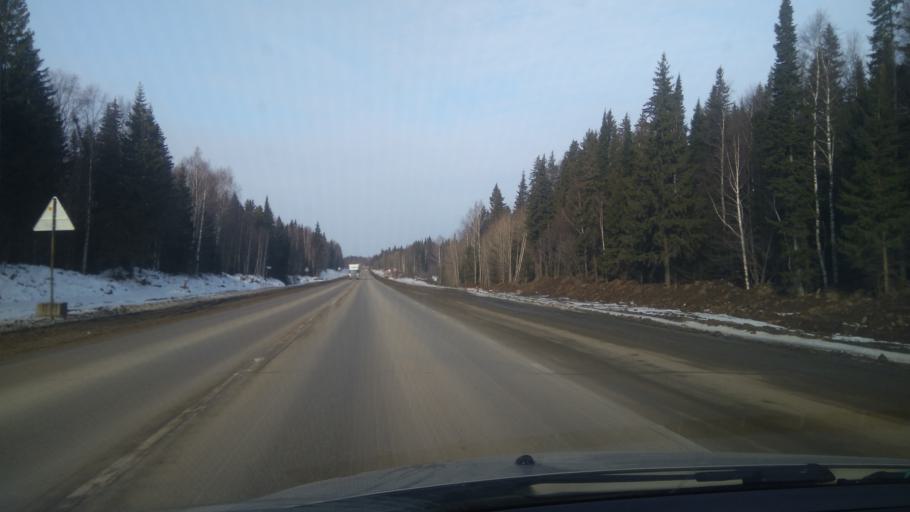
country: RU
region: Sverdlovsk
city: Bisert'
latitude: 56.8276
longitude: 59.1469
